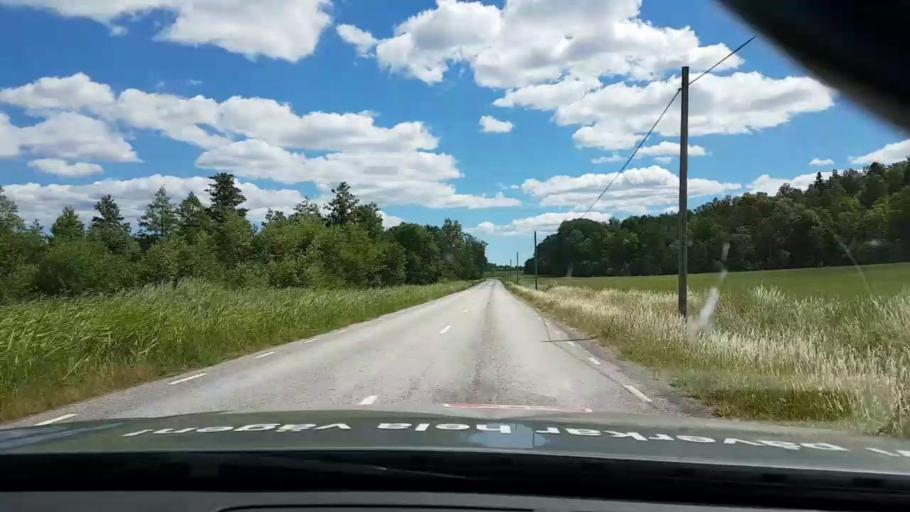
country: SE
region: Kalmar
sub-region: Vasterviks Kommun
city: Forserum
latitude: 58.0441
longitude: 16.4185
